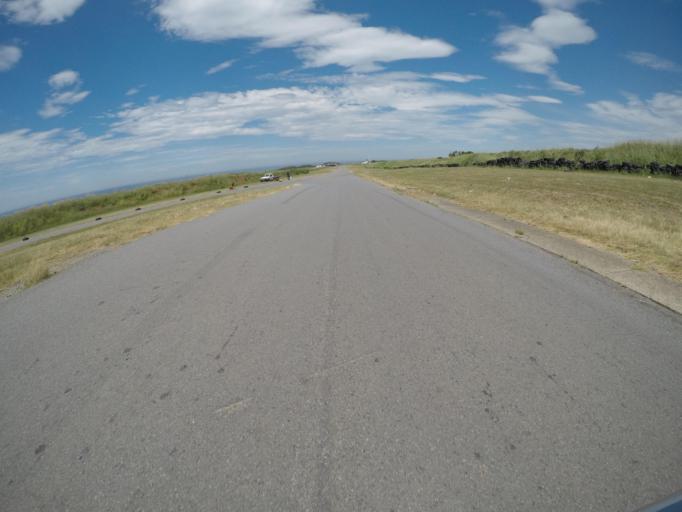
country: ZA
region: Eastern Cape
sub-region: Buffalo City Metropolitan Municipality
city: East London
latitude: -33.0443
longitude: 27.8726
